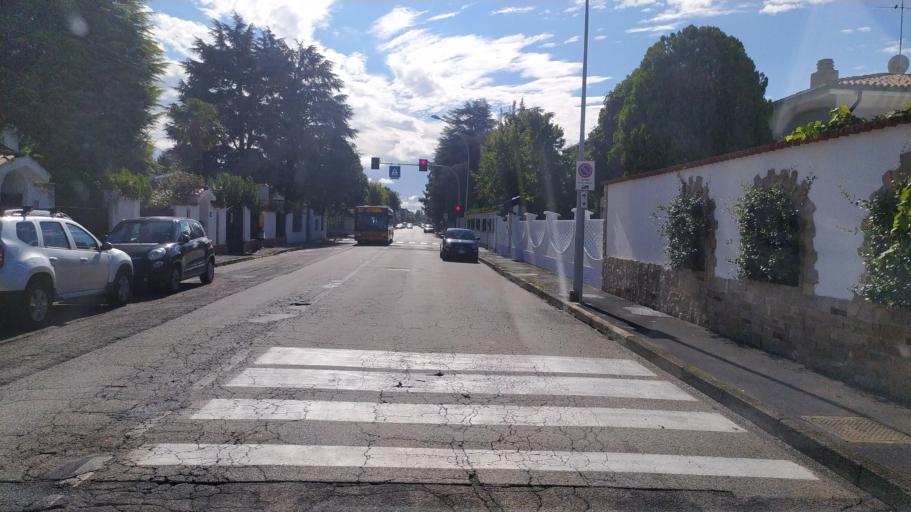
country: IT
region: Lombardy
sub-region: Citta metropolitana di Milano
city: Trezzano sul Naviglio
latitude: 45.4255
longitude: 9.0511
